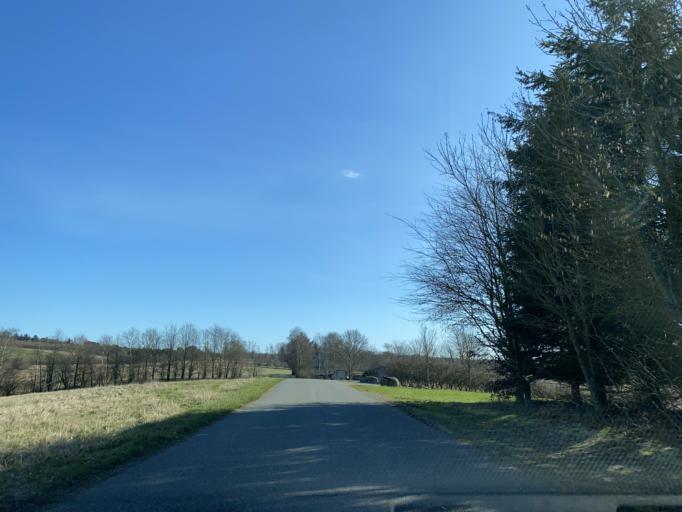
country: DK
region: Central Jutland
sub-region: Arhus Kommune
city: Framlev
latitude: 56.1816
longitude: 10.0260
